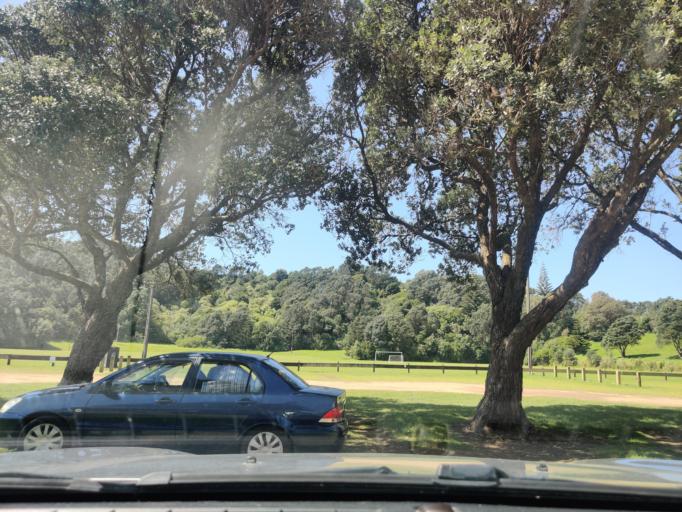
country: NZ
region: Taranaki
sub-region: New Plymouth District
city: New Plymouth
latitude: -39.1112
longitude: 173.9574
